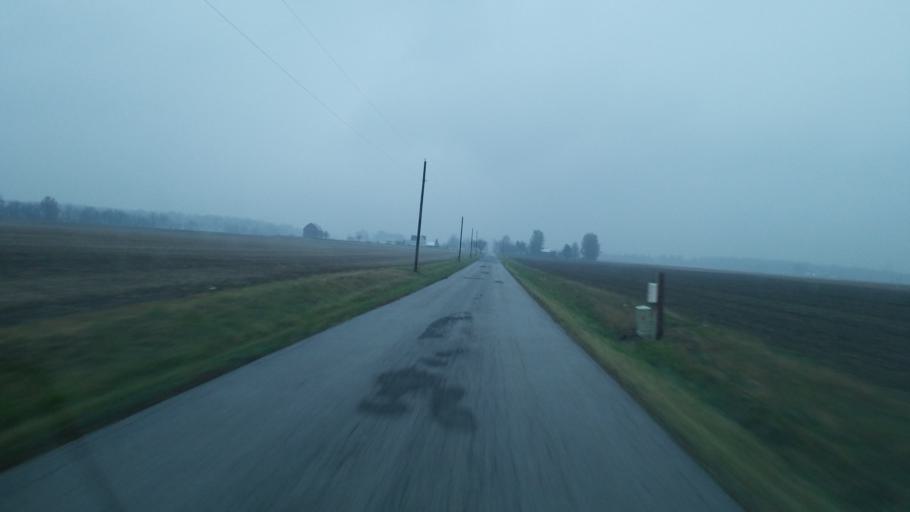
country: US
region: Ohio
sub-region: Morrow County
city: Cardington
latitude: 40.4627
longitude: -82.9049
